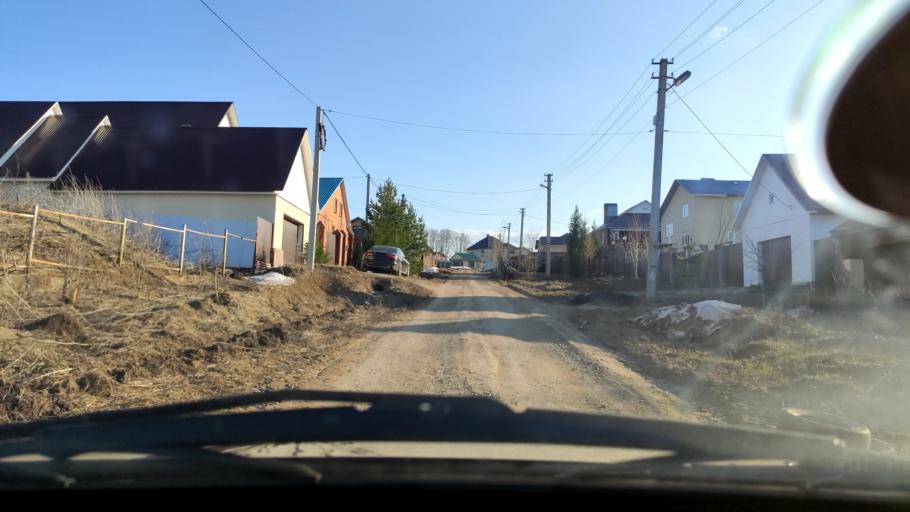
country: RU
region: Bashkortostan
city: Kabakovo
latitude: 54.6331
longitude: 56.0667
